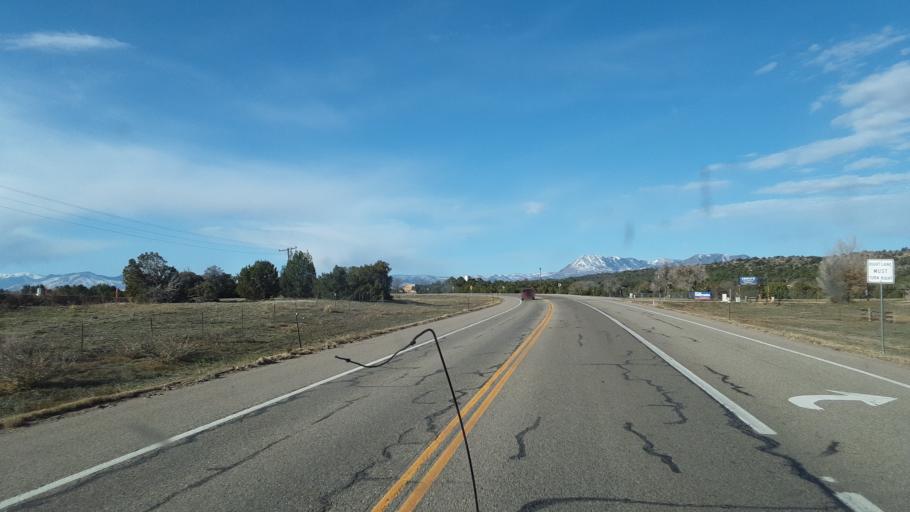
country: US
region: Colorado
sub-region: Huerfano County
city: Walsenburg
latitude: 37.5979
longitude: -104.8578
